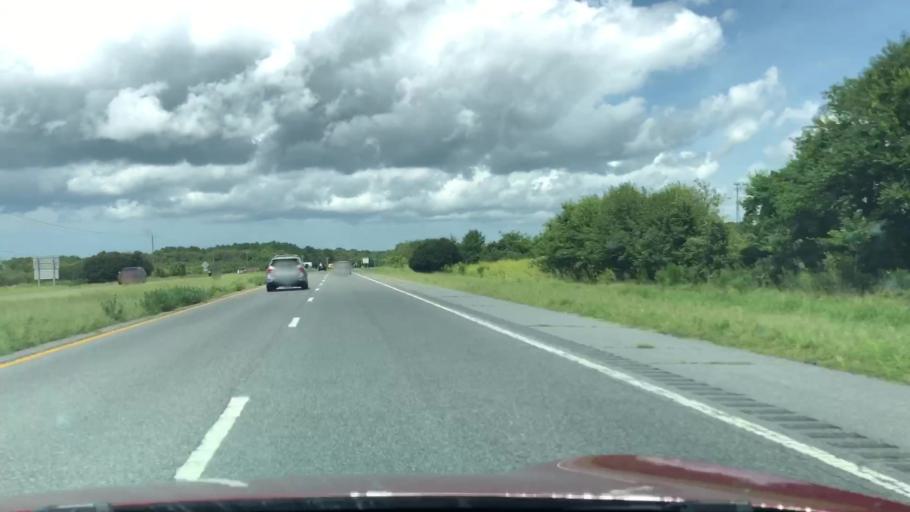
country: US
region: Virginia
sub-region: Northampton County
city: Cape Charles
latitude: 37.1431
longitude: -75.9681
